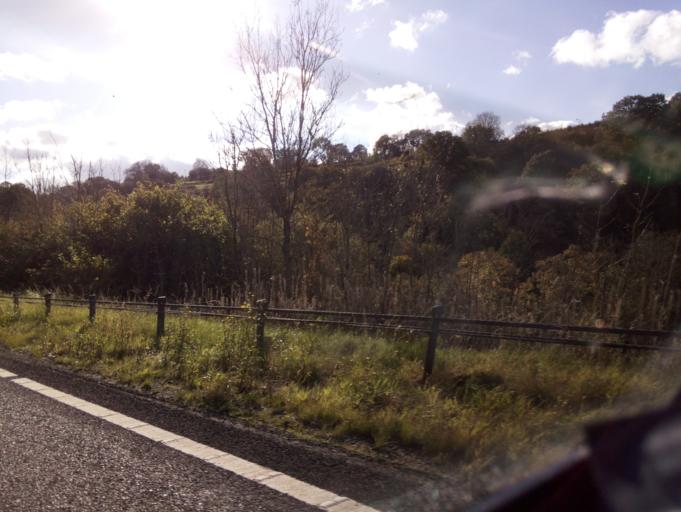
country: GB
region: Wales
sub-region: Merthyr Tydfil County Borough
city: Merthyr Tydfil
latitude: 51.7705
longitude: -3.4175
